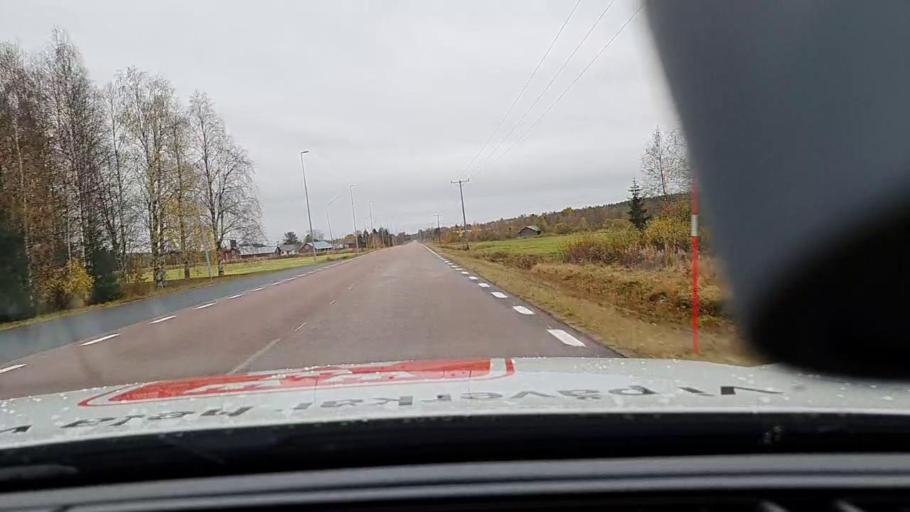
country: FI
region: Lapland
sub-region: Torniolaakso
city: Ylitornio
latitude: 66.1410
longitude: 23.8994
